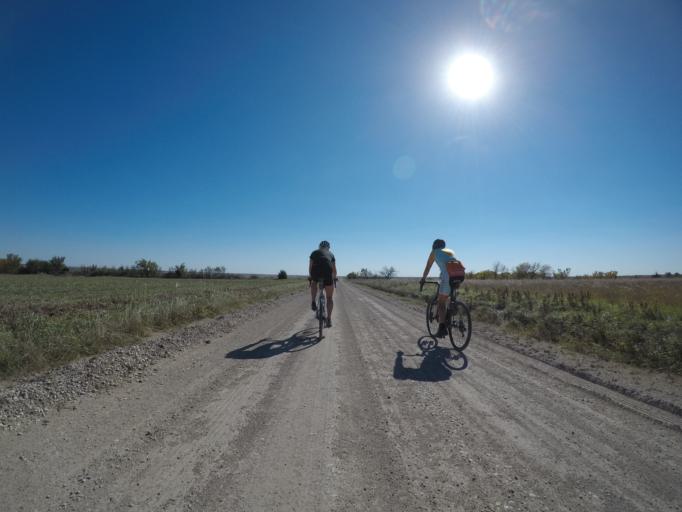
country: US
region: Kansas
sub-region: Wabaunsee County
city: Alma
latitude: 38.9684
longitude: -96.4734
